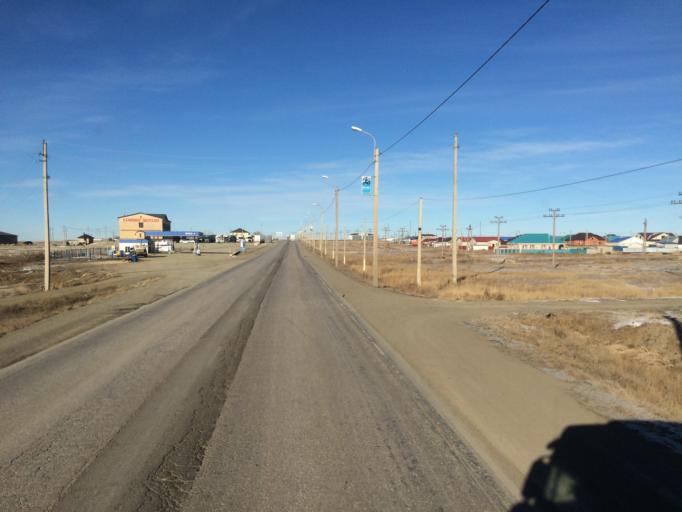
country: KZ
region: Aqtoebe
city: Khromtau
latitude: 50.2522
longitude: 58.4197
